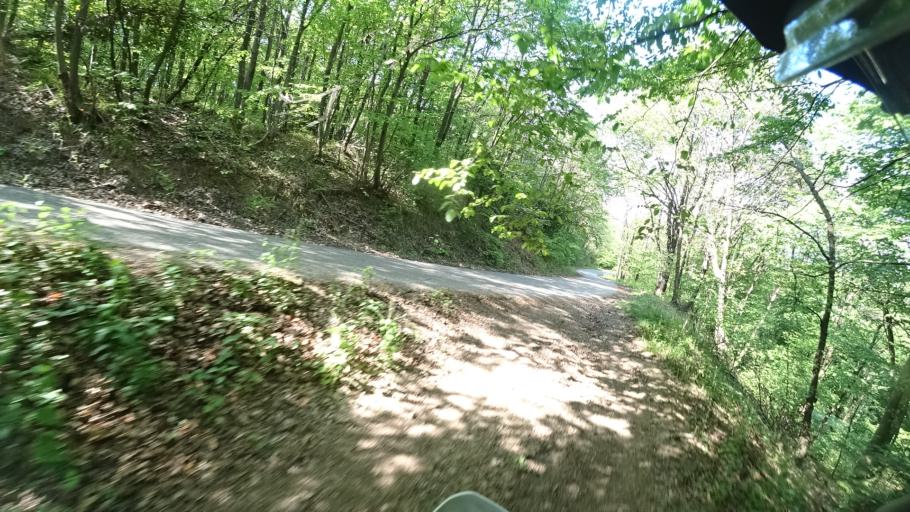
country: HR
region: Grad Zagreb
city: Kasina
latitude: 45.9459
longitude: 15.9683
